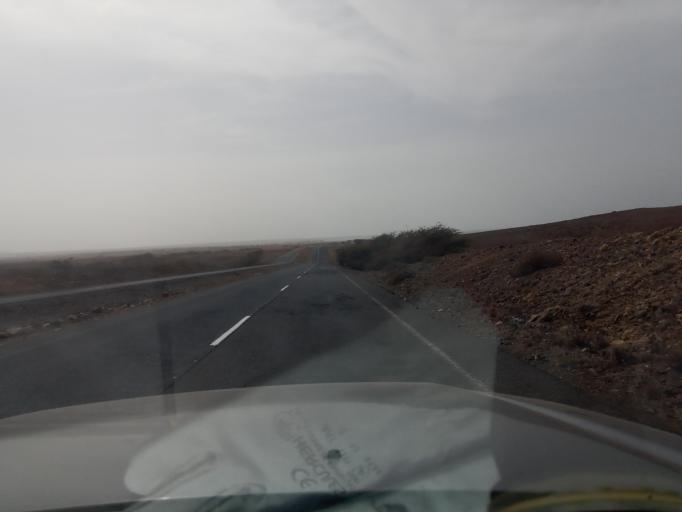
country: CV
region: Sal
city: Espargos
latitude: 16.7149
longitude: -22.9396
